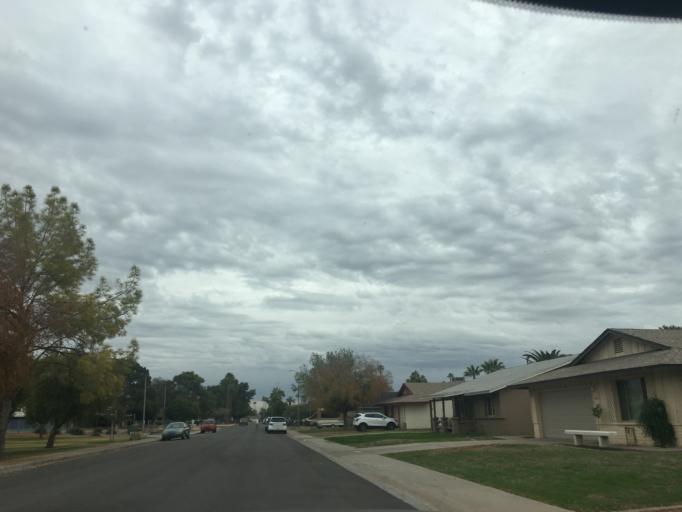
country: US
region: Arizona
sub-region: Maricopa County
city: Tempe
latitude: 33.3841
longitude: -111.9018
